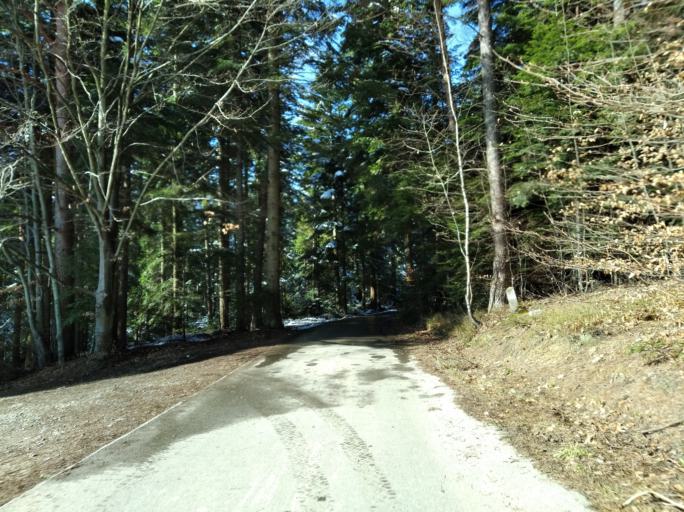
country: PL
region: Subcarpathian Voivodeship
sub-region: Powiat krosnienski
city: Korczyna
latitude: 49.7413
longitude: 21.8308
